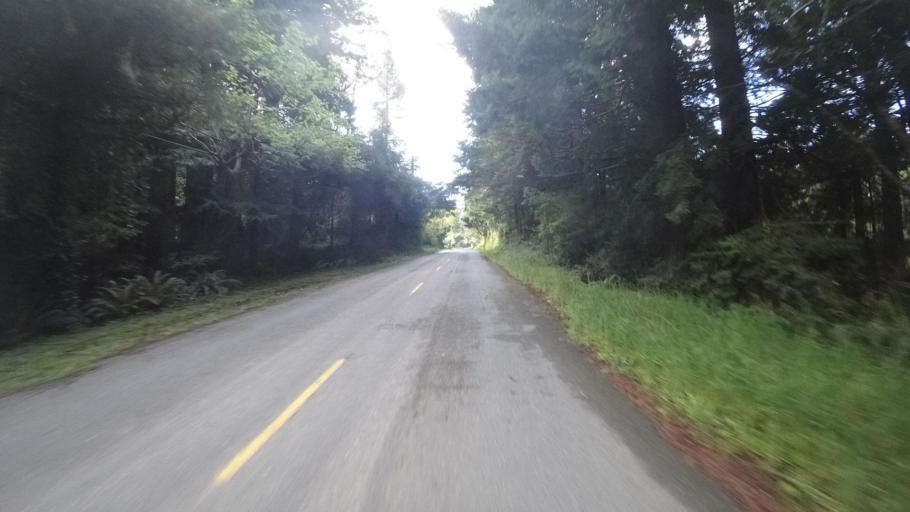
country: US
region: California
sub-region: Humboldt County
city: Westhaven-Moonstone
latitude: 41.0563
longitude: -124.1244
